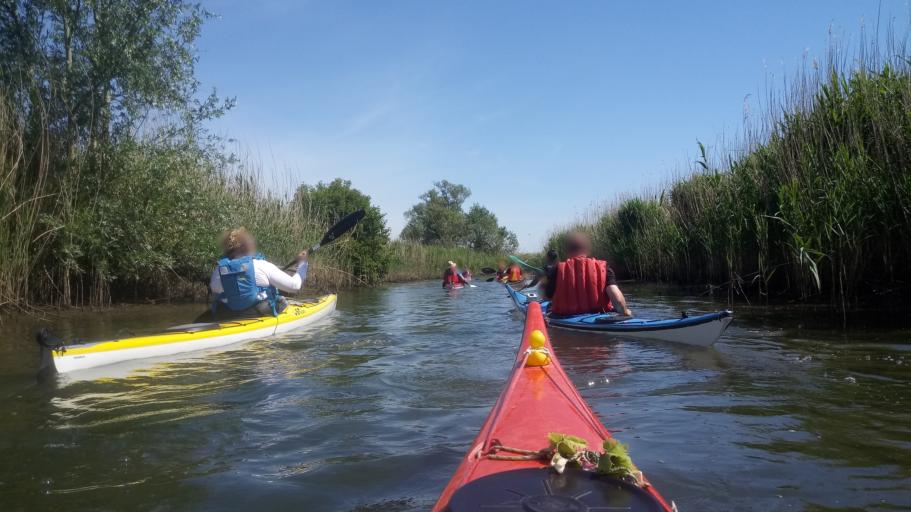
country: NL
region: North Brabant
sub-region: Gemeente Geertruidenberg
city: Geertruidenberg
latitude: 51.7388
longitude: 4.8451
